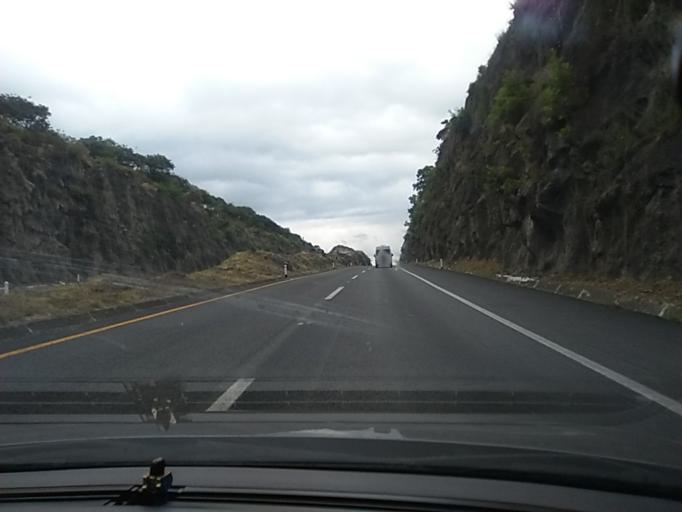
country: MX
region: Jalisco
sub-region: Zapotlan del Rey
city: Zapotlan del Rey
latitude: 20.5156
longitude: -102.9757
